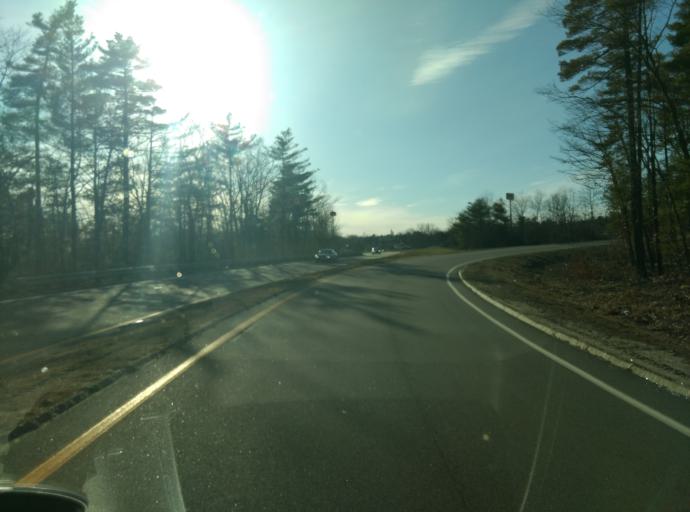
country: US
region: Massachusetts
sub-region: Middlesex County
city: Tewksbury
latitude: 42.6407
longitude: -71.2321
